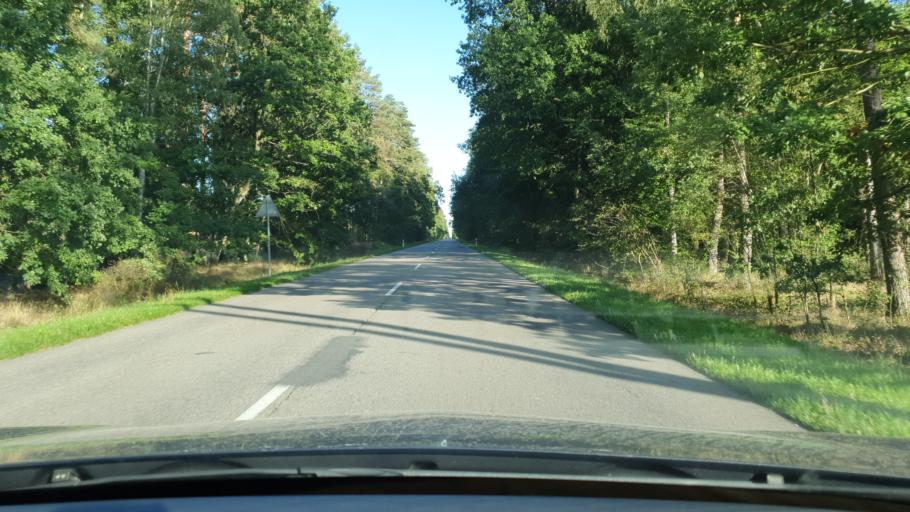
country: PL
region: West Pomeranian Voivodeship
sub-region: Powiat kamienski
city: Golczewo
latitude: 53.8146
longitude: 15.0646
